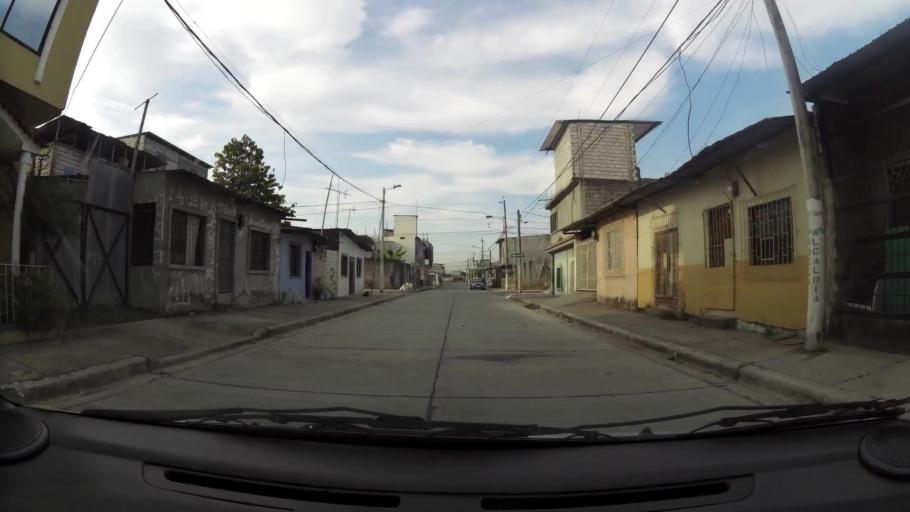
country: EC
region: Guayas
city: Eloy Alfaro
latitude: -2.0896
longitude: -79.9015
